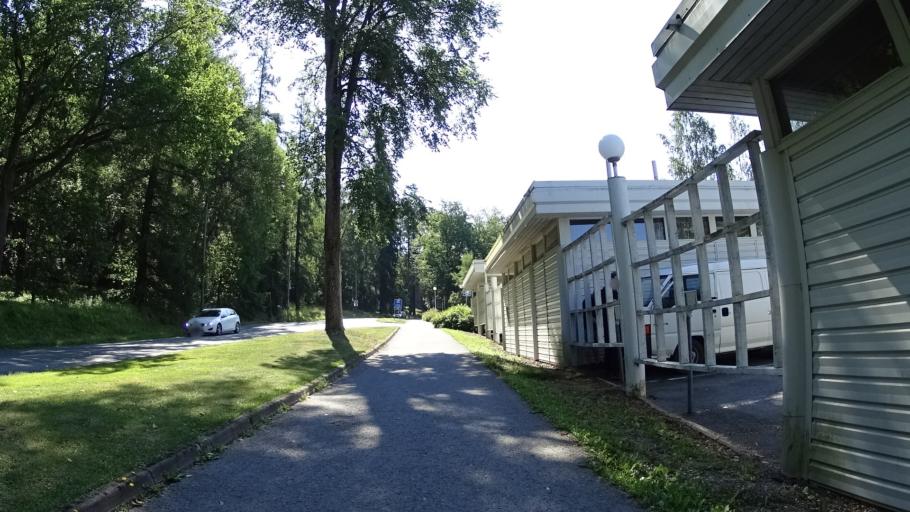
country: FI
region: Haeme
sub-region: Haemeenlinna
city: Haemeenlinna
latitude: 61.0236
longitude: 24.4460
